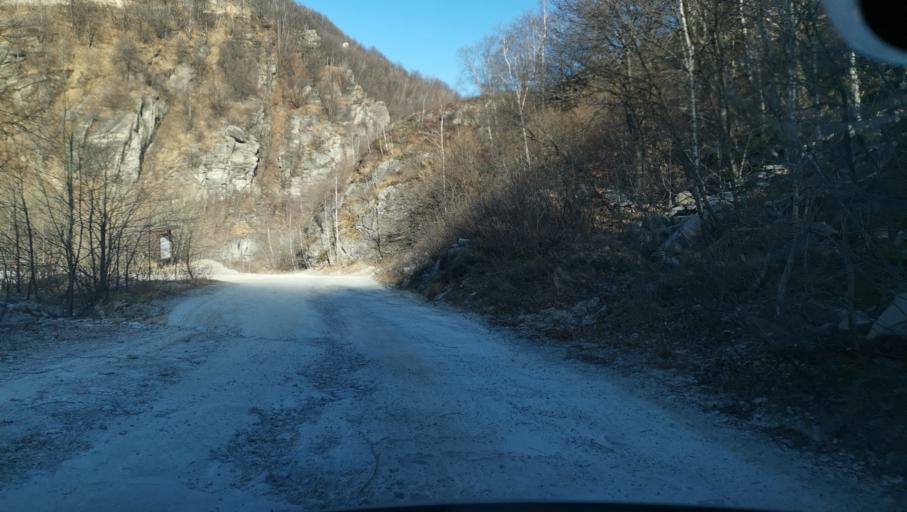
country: IT
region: Piedmont
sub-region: Provincia di Torino
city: Rora
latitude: 44.7651
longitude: 7.2005
